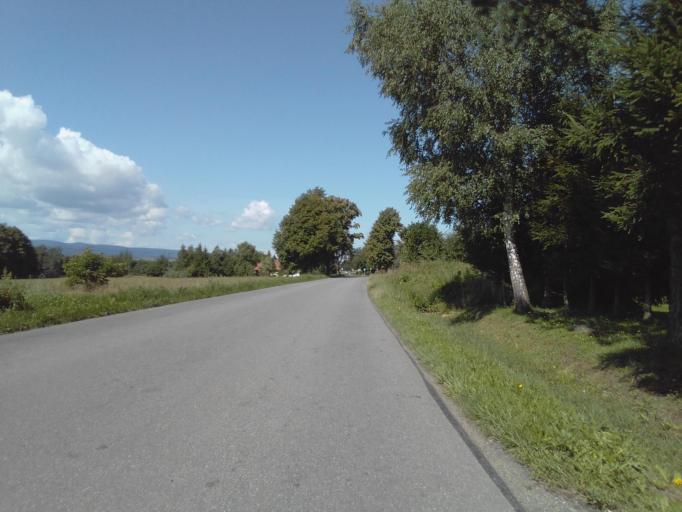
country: PL
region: Subcarpathian Voivodeship
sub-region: Powiat jasielski
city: Nowy Zmigrod
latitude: 49.6134
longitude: 21.5932
